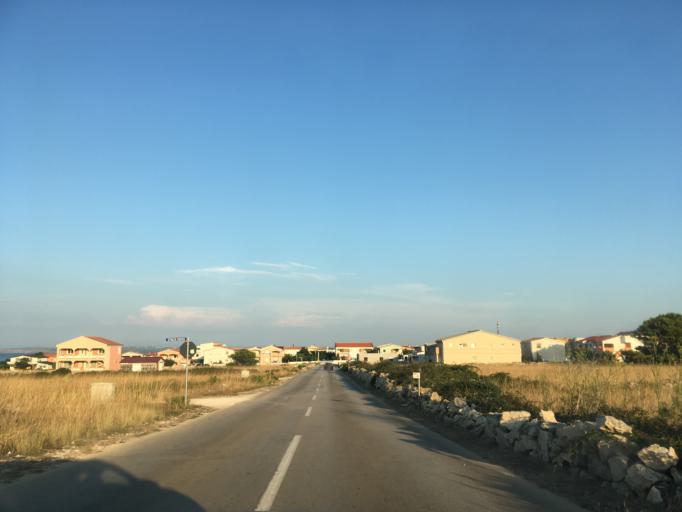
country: HR
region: Zadarska
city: Vir
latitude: 44.2979
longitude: 15.1154
